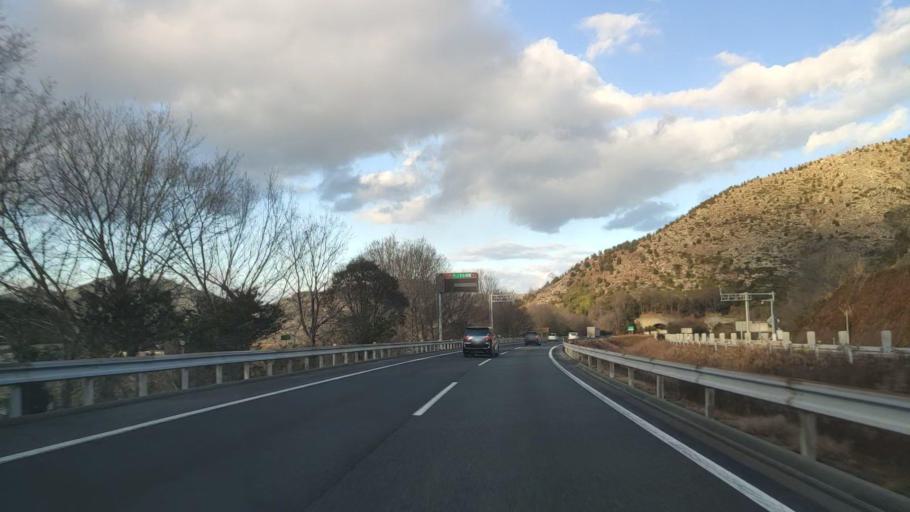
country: JP
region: Hyogo
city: Kariya
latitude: 34.7846
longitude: 134.3980
